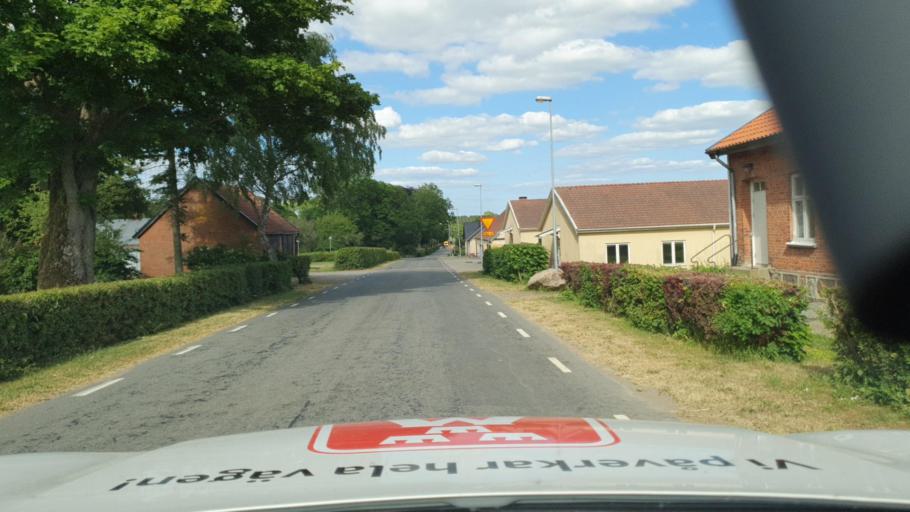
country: SE
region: Skane
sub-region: Tomelilla Kommun
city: Tomelilla
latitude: 55.4888
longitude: 14.0444
